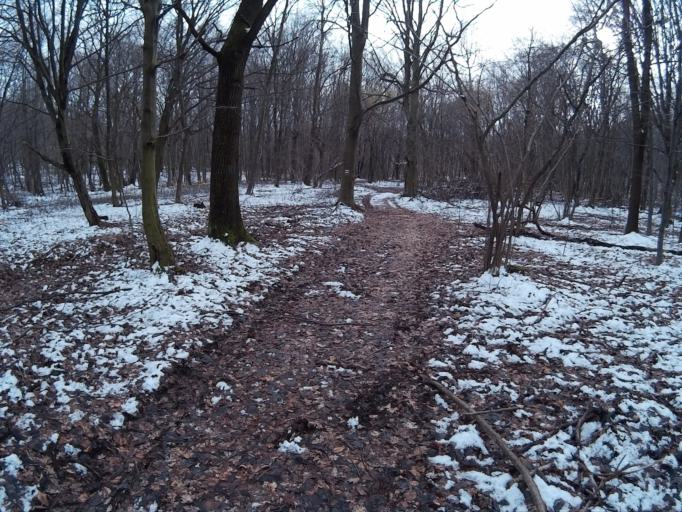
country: HU
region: Borsod-Abauj-Zemplen
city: Gonc
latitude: 48.4141
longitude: 21.3516
